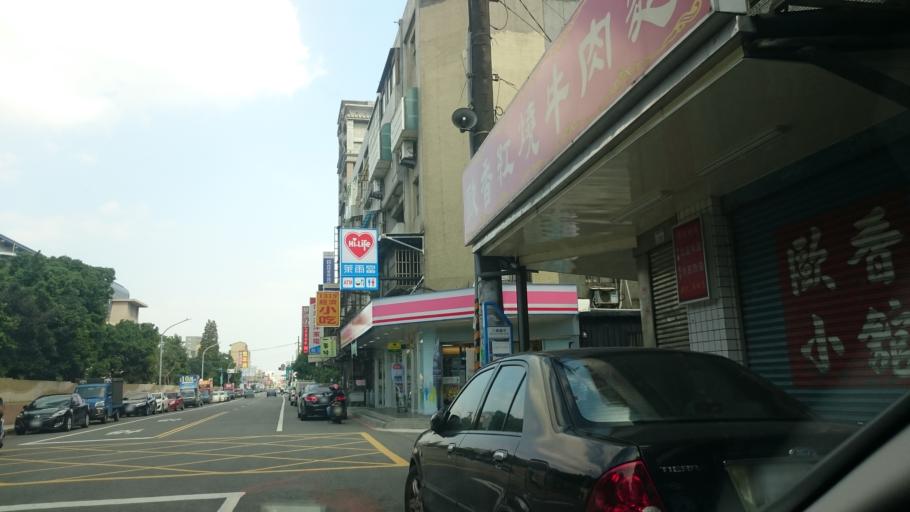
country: TW
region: Taiwan
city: Daxi
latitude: 24.9293
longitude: 121.2872
